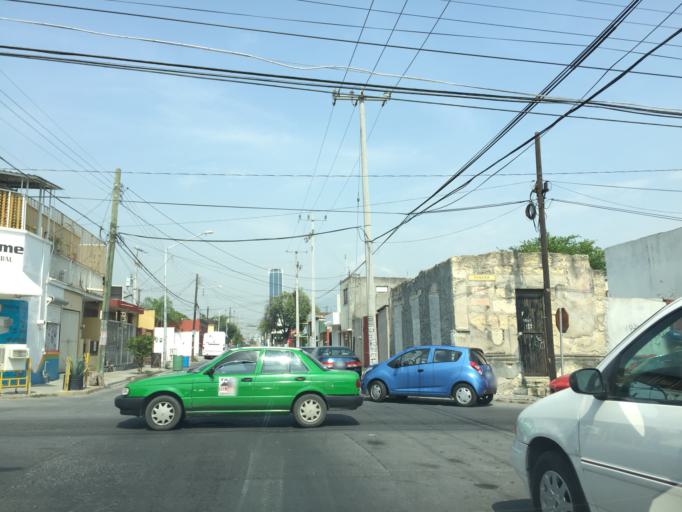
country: MX
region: Nuevo Leon
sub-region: Monterrey
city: Monterrey
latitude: 25.6617
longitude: -100.3018
